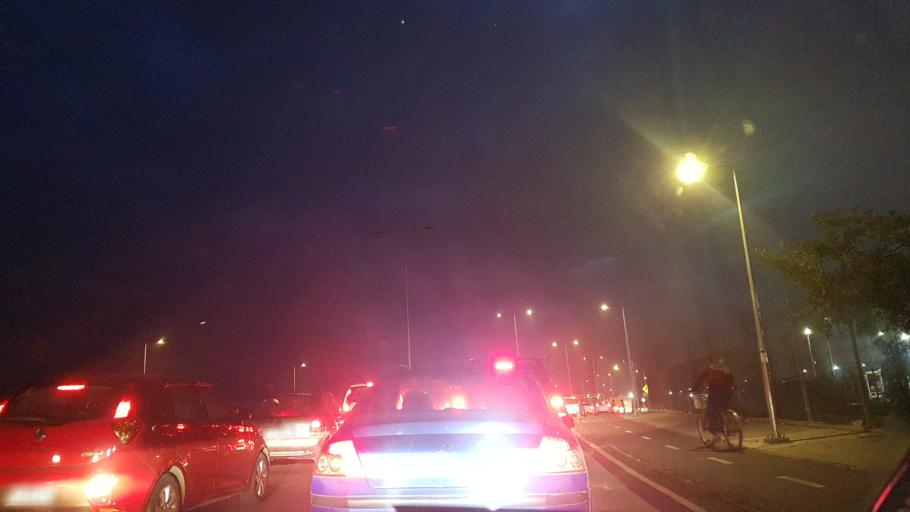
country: CL
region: Santiago Metropolitan
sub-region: Provincia de Santiago
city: Lo Prado
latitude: -33.3564
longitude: -70.7099
